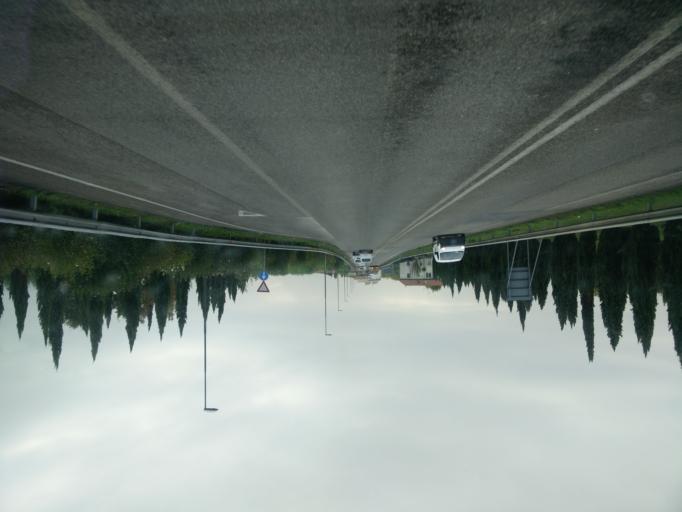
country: IT
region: Tuscany
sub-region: Province of Florence
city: Campi Bisenzio
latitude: 43.8304
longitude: 11.1369
